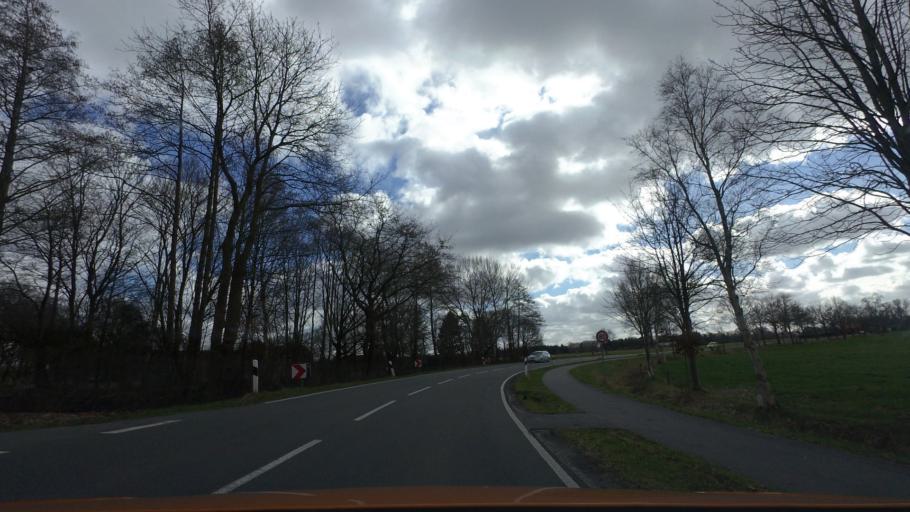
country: DE
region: Lower Saxony
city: Bad Zwischenahn
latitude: 53.1560
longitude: 8.0902
